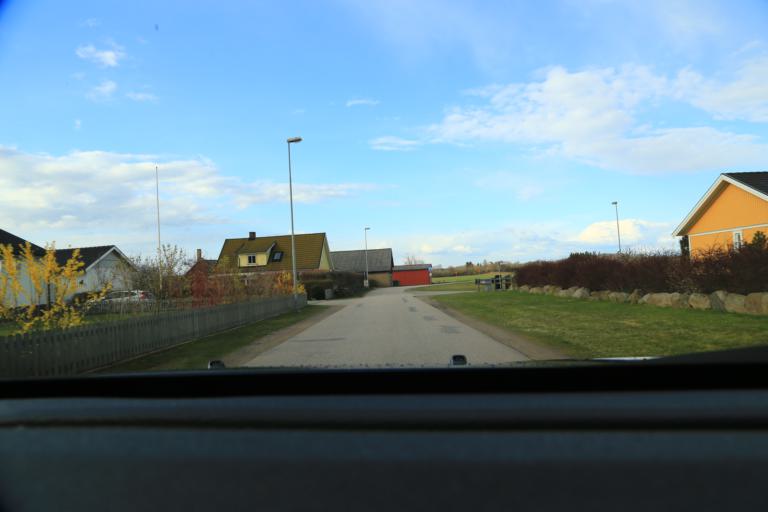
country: SE
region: Halland
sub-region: Varbergs Kommun
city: Traslovslage
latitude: 57.0483
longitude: 12.2949
